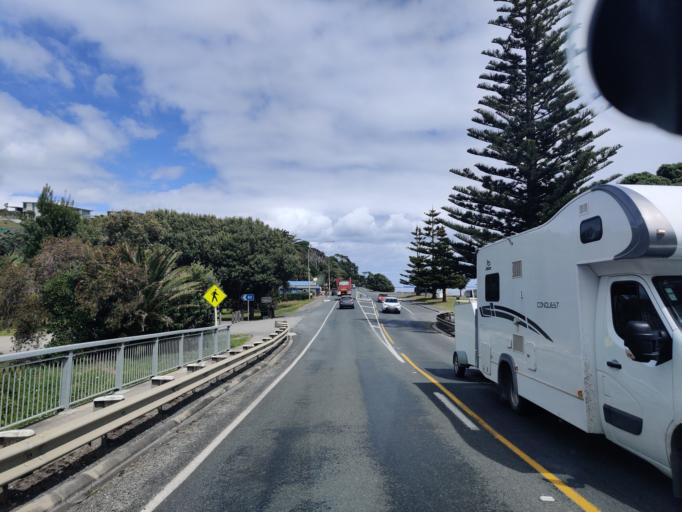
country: NZ
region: Northland
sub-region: Far North District
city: Taipa
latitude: -34.9912
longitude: 173.4850
